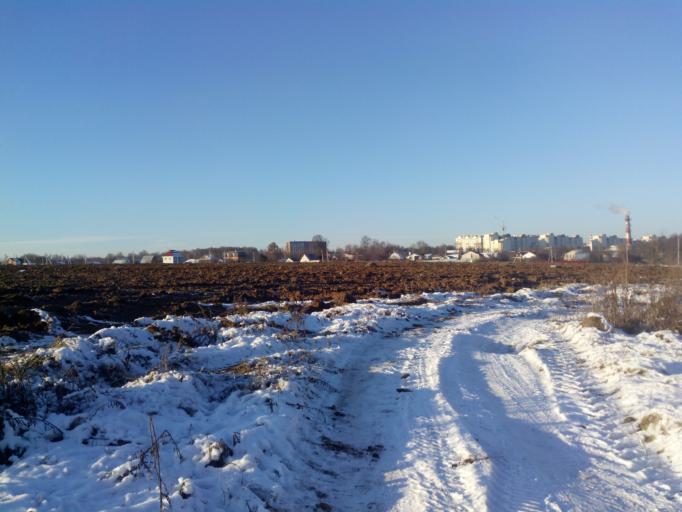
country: RU
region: Moskovskaya
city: Yakovlevskoye
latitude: 55.4950
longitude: 37.9534
